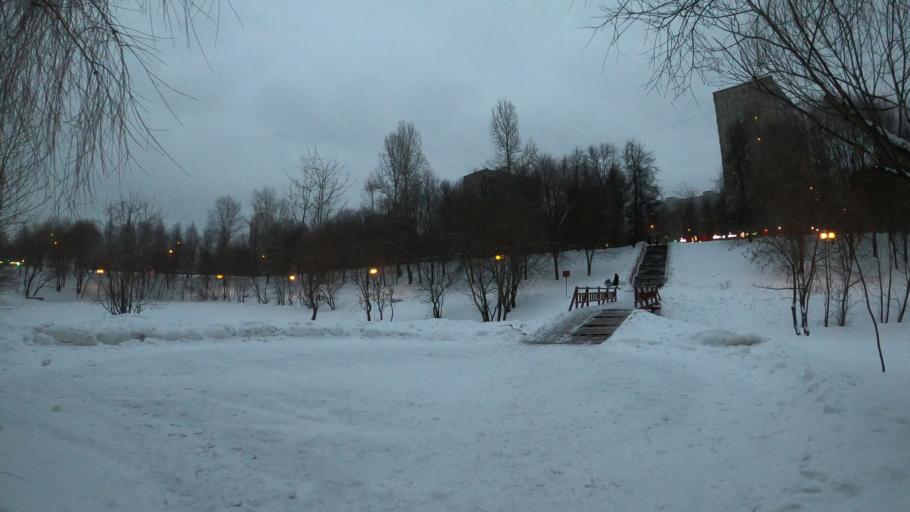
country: RU
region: Moscow
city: Chertanovo Yuzhnoye
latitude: 55.6062
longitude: 37.5873
